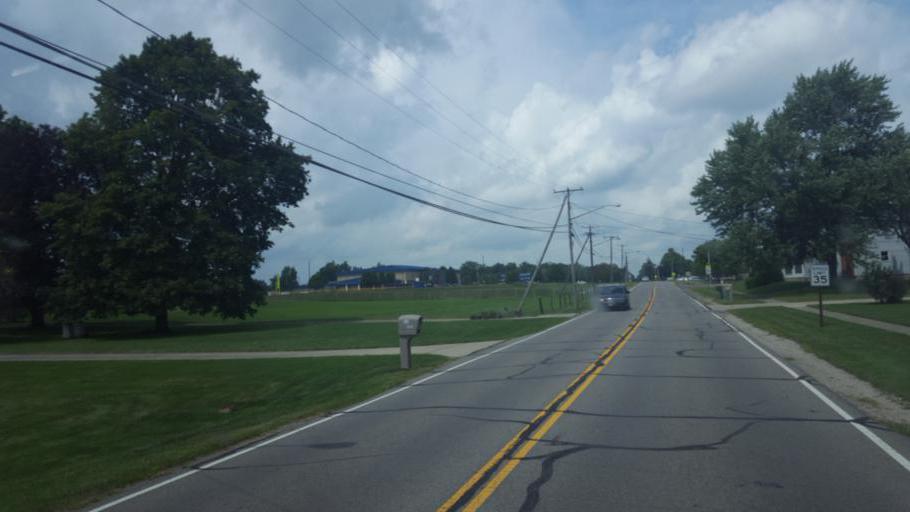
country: US
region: Ohio
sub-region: Richland County
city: Ontario
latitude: 40.7616
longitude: -82.6451
